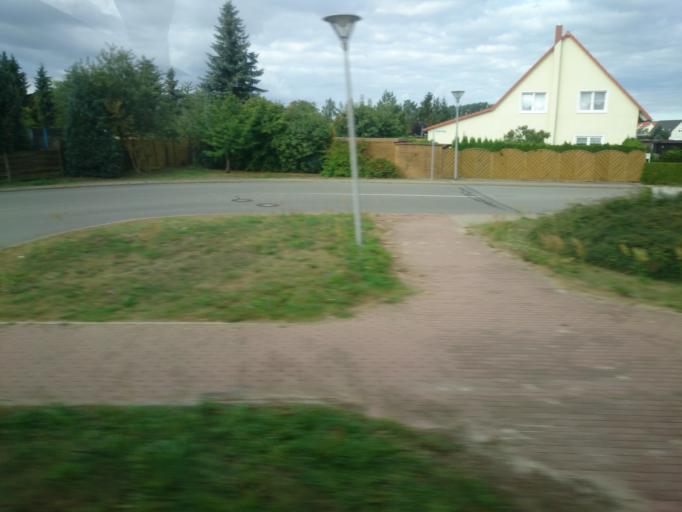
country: DE
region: Mecklenburg-Vorpommern
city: Pasewalk
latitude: 53.5228
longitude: 13.9764
